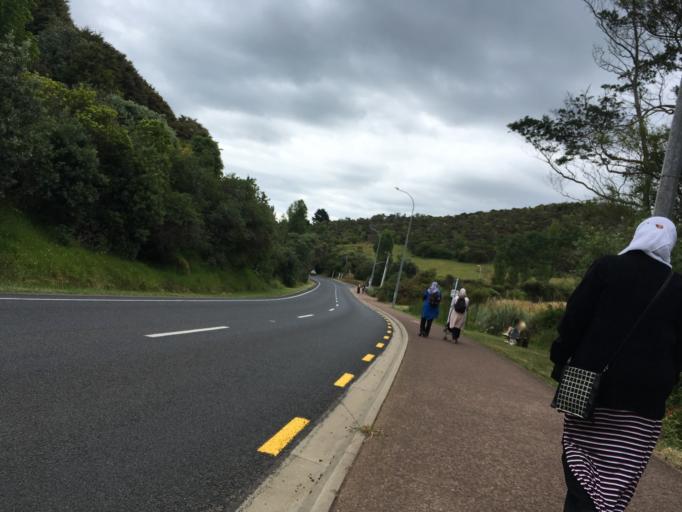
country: NZ
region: Auckland
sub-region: Auckland
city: Pakuranga
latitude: -36.7818
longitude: 175.0007
